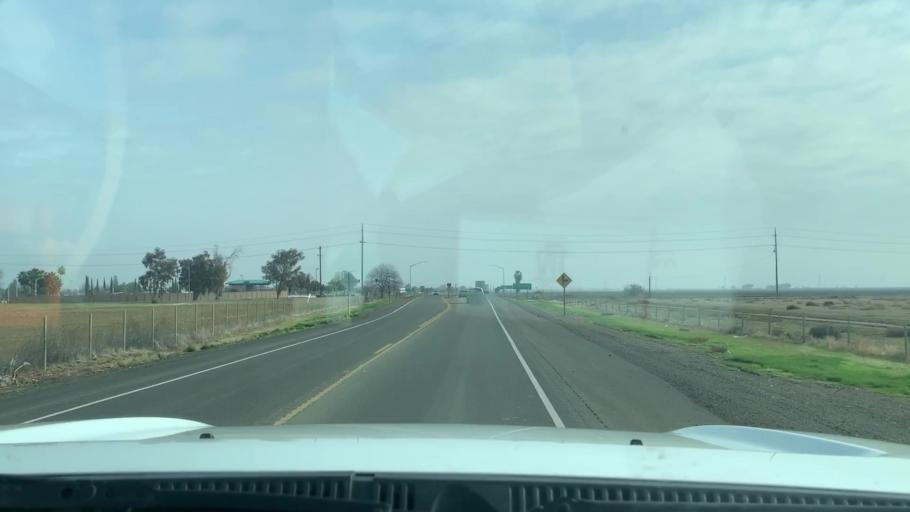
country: US
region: California
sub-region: Kings County
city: Lemoore Station
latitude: 36.2553
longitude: -119.9077
